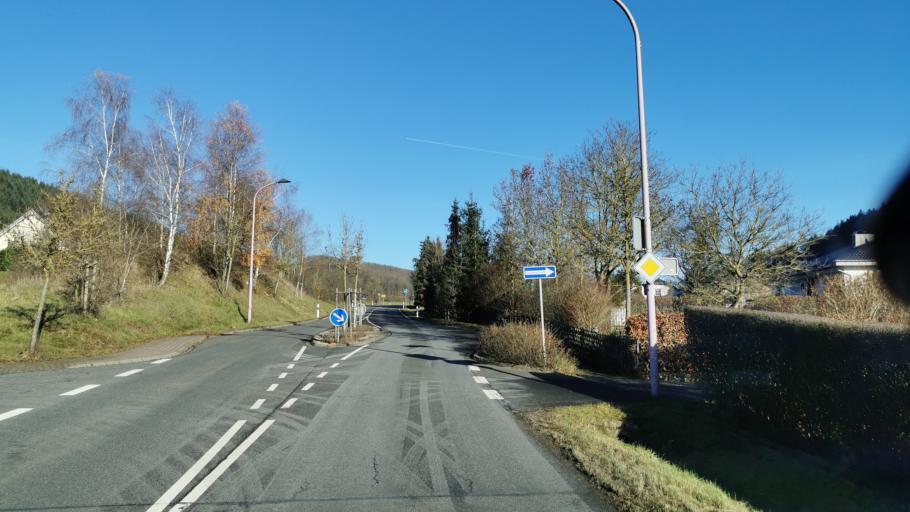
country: DE
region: Rheinland-Pfalz
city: Oberstadtfeld
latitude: 50.1771
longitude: 6.7725
